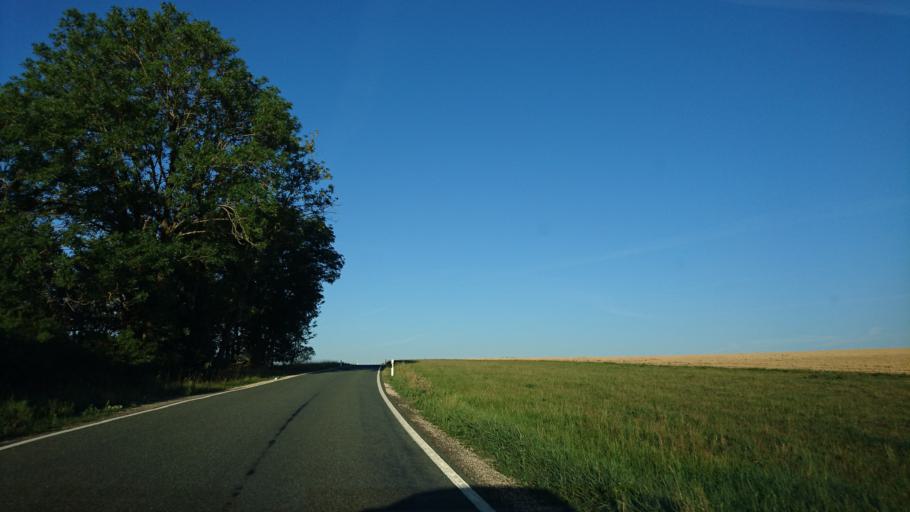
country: DE
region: Bavaria
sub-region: Regierungsbezirk Mittelfranken
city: Nennslingen
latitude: 49.0512
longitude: 11.1580
